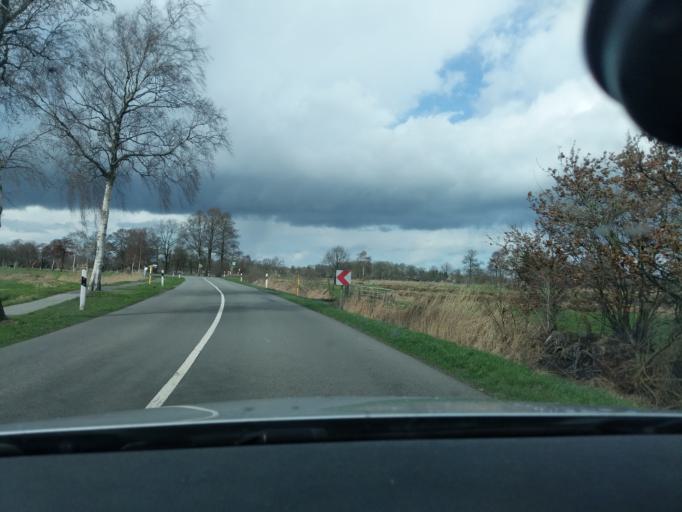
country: DE
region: Lower Saxony
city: Stade
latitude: 53.6244
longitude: 9.4400
